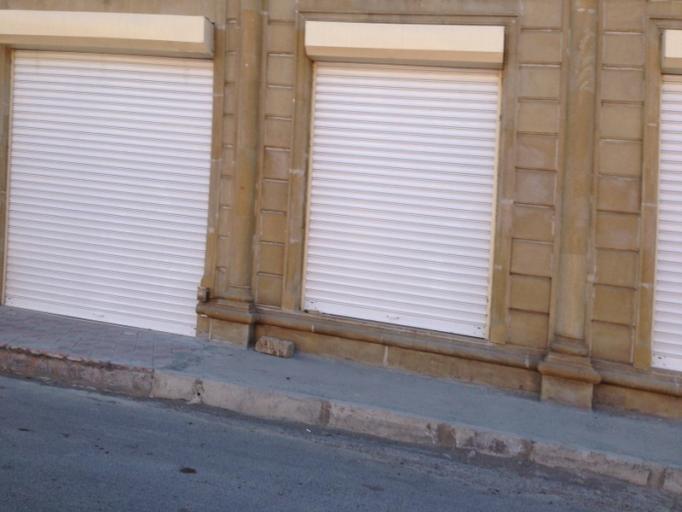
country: AZ
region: Baki
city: Baku
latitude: 40.4228
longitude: 49.8624
